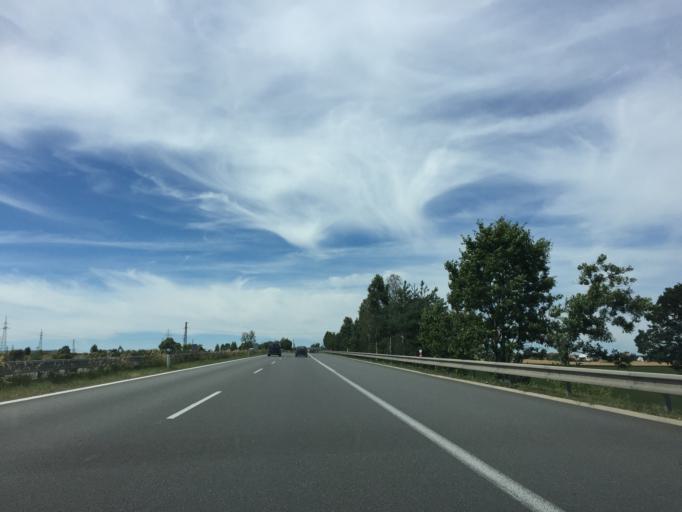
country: CZ
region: Jihocesky
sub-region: Okres Tabor
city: Sezimovo Usti
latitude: 49.4129
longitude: 14.7114
